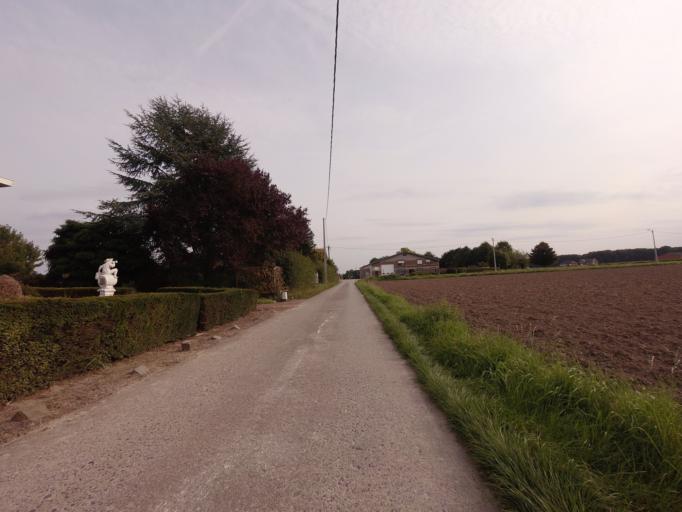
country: BE
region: Flanders
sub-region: Provincie Vlaams-Brabant
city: Kampenhout
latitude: 50.9439
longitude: 4.5381
